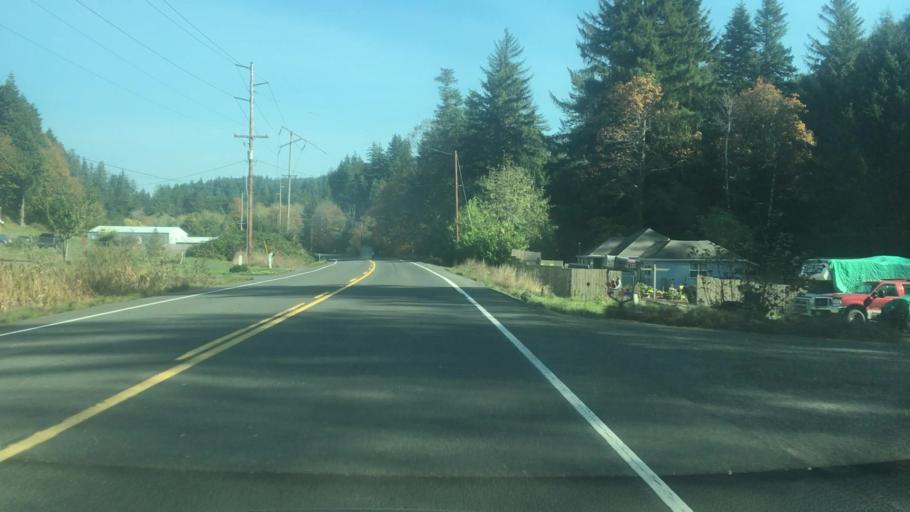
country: US
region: Oregon
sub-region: Lincoln County
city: Rose Lodge
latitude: 45.0224
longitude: -123.8337
